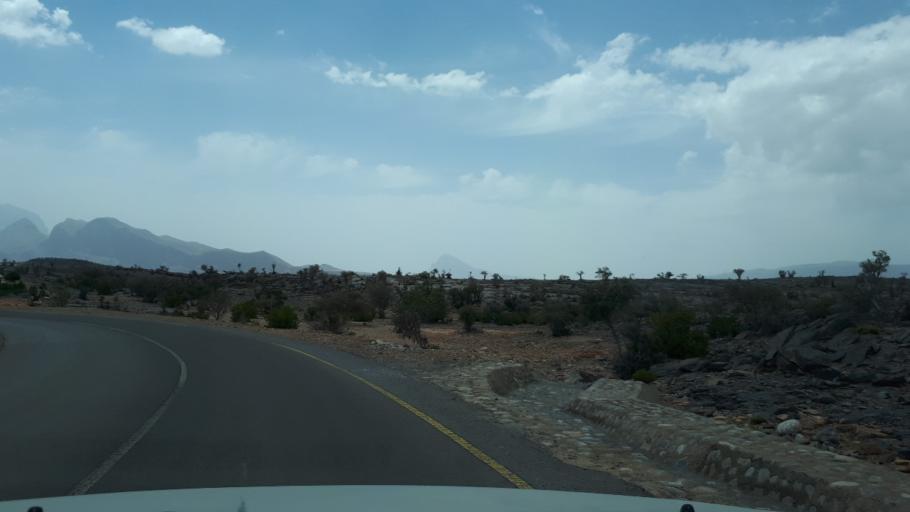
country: OM
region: Muhafazat ad Dakhiliyah
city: Bahla'
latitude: 23.2092
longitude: 57.1994
